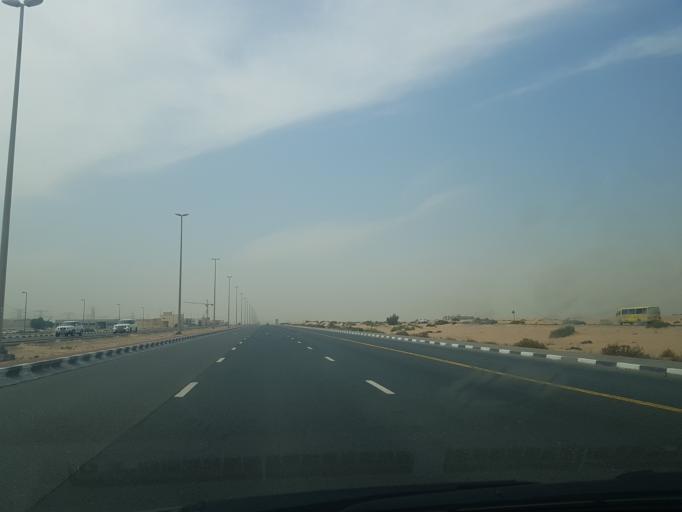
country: AE
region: Ash Shariqah
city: Sharjah
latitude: 25.2549
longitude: 55.5228
